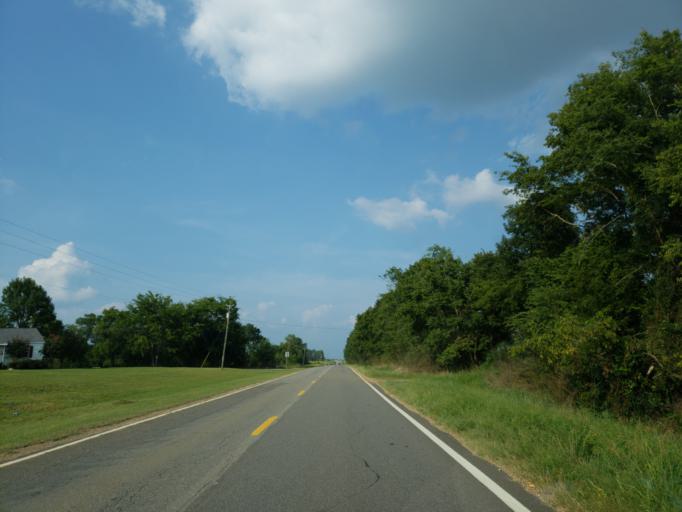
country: US
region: Alabama
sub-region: Greene County
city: Eutaw
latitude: 32.7999
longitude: -87.9617
